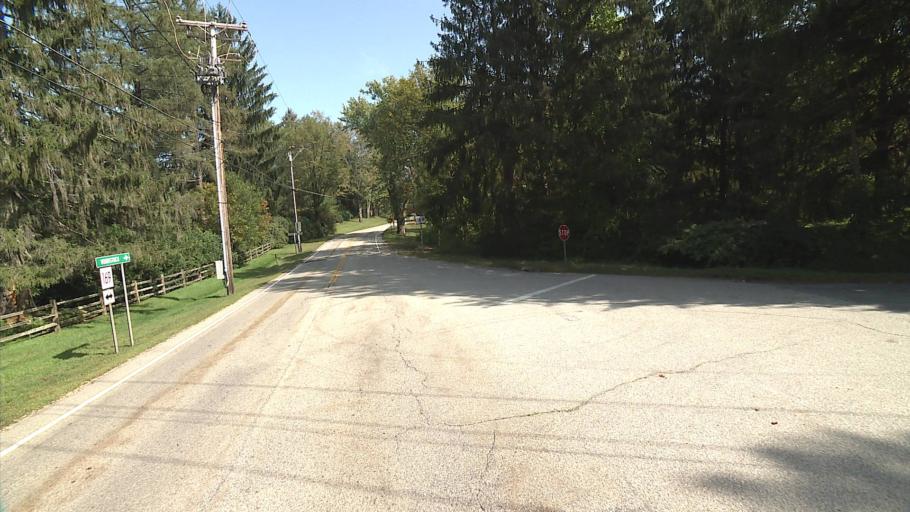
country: US
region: Connecticut
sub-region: Windham County
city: South Woodstock
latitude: 41.9037
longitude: -71.9593
